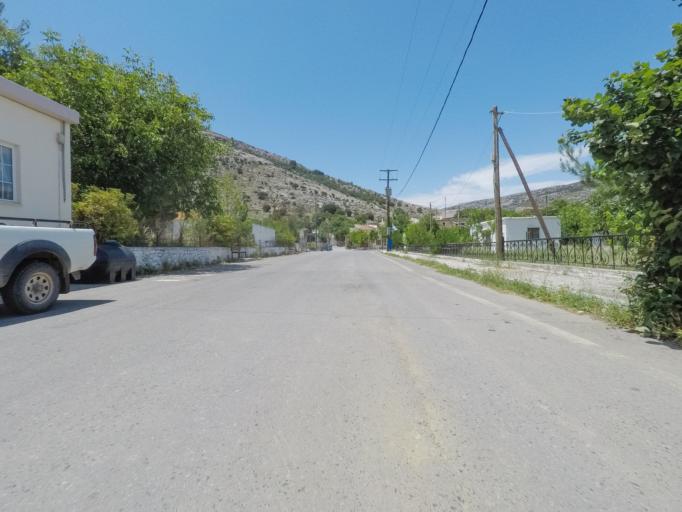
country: GR
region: Crete
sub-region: Nomos Irakleiou
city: Mokhos
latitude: 35.1845
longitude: 25.4323
